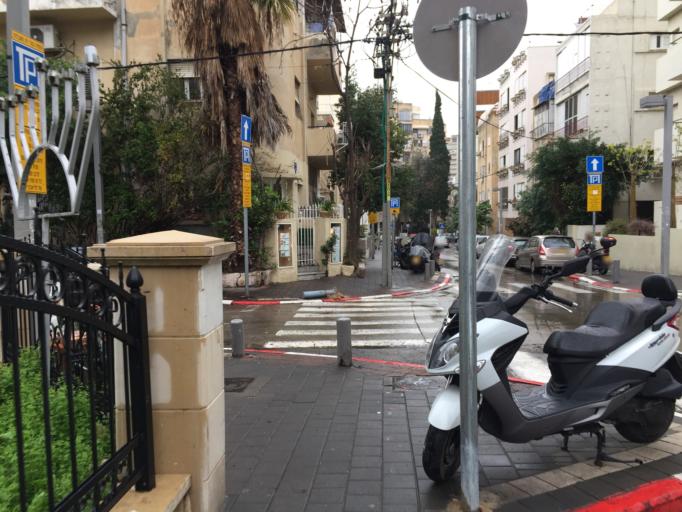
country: IL
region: Tel Aviv
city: Tel Aviv
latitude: 32.0696
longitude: 34.7734
